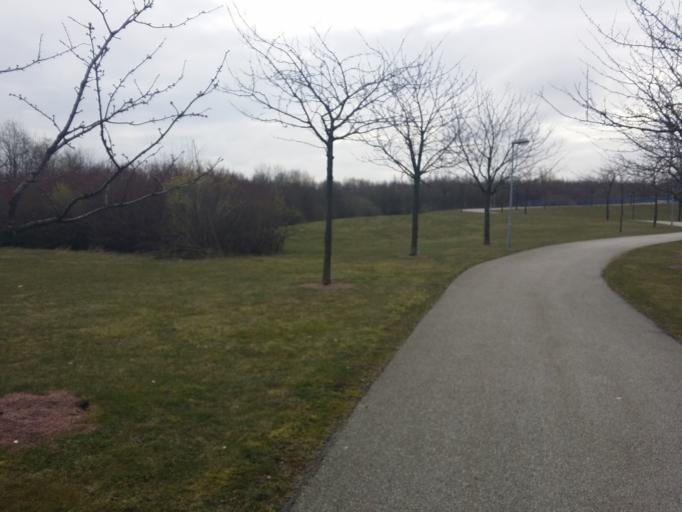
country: SE
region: Skane
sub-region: Burlovs Kommun
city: Arloev
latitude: 55.6095
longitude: 13.0840
